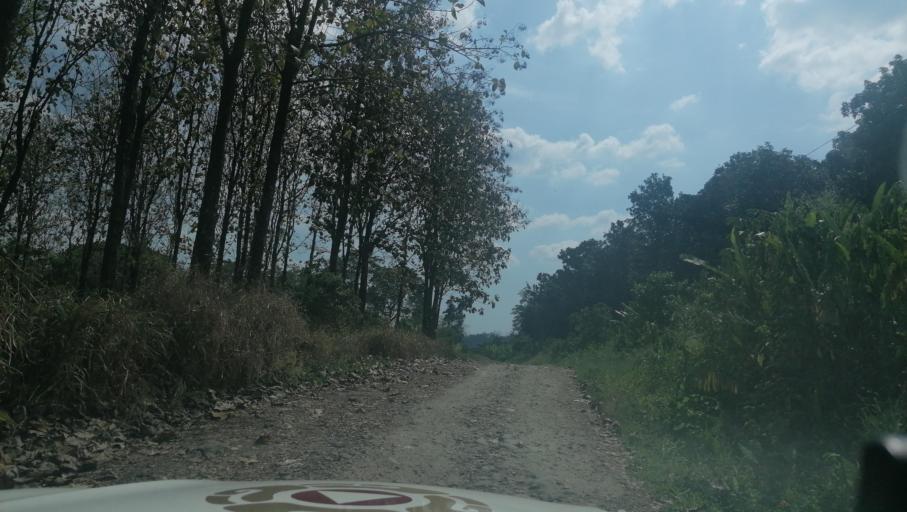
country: MX
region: Chiapas
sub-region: Cacahoatan
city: Benito Juarez
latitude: 15.0257
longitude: -92.2377
